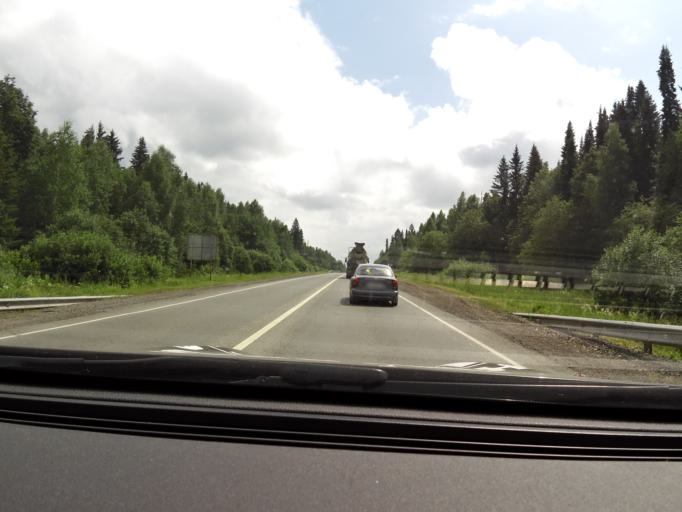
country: RU
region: Perm
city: Kungur
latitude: 57.3243
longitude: 56.9611
